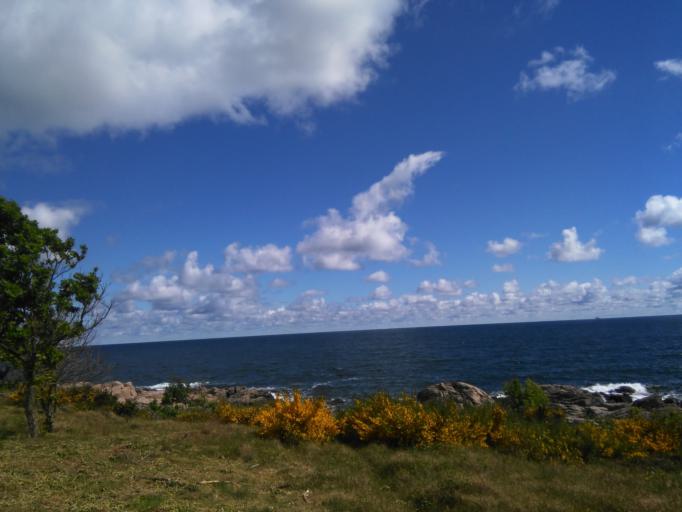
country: DK
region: Capital Region
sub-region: Bornholm Kommune
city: Ronne
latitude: 55.2950
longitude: 14.7777
